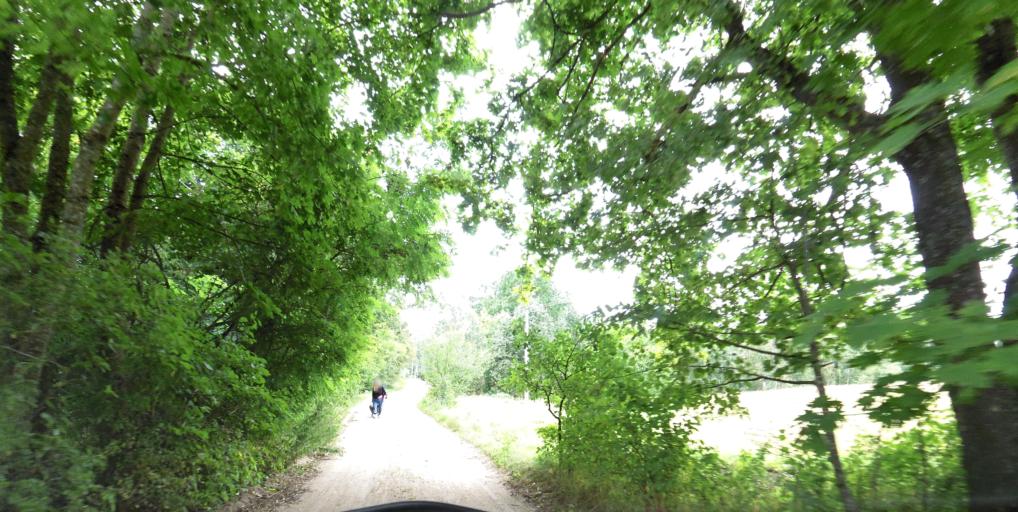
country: LT
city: Grigiskes
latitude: 54.7623
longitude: 25.0223
